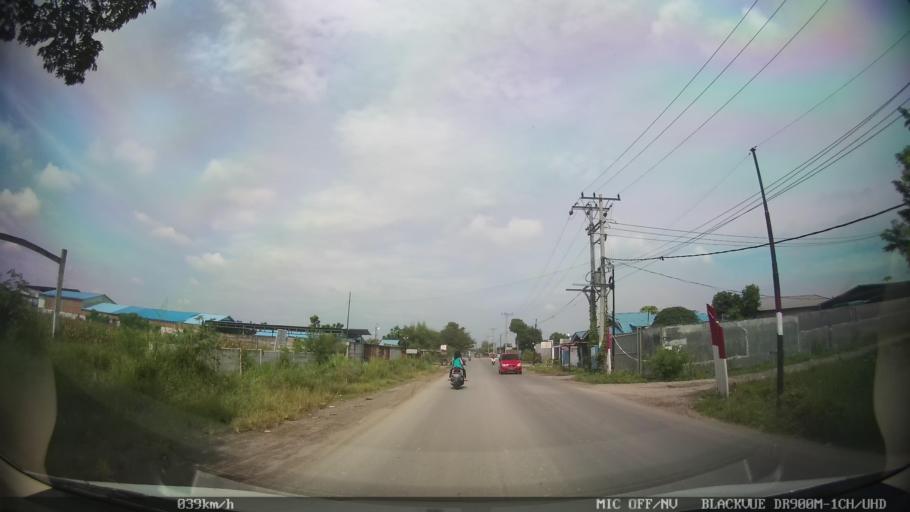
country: ID
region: North Sumatra
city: Medan
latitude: 3.6504
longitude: 98.7127
